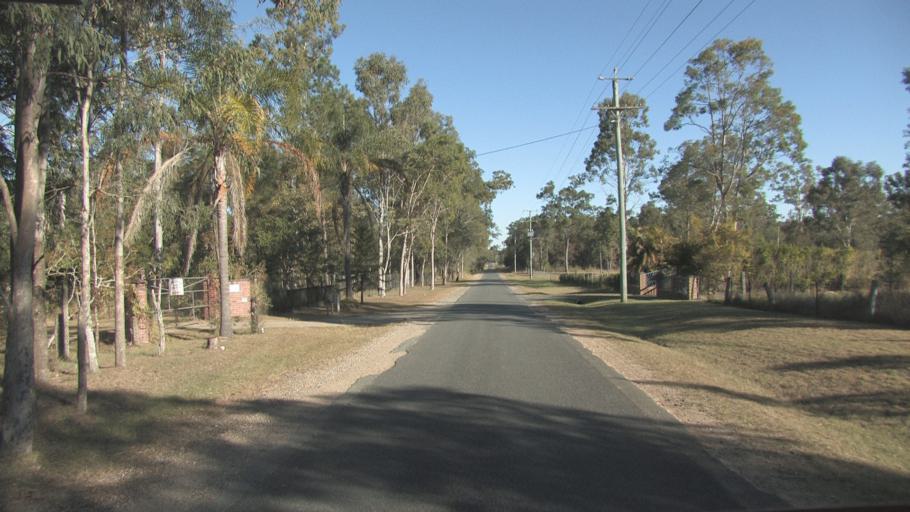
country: AU
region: Queensland
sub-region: Logan
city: North Maclean
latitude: -27.7846
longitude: 153.0392
